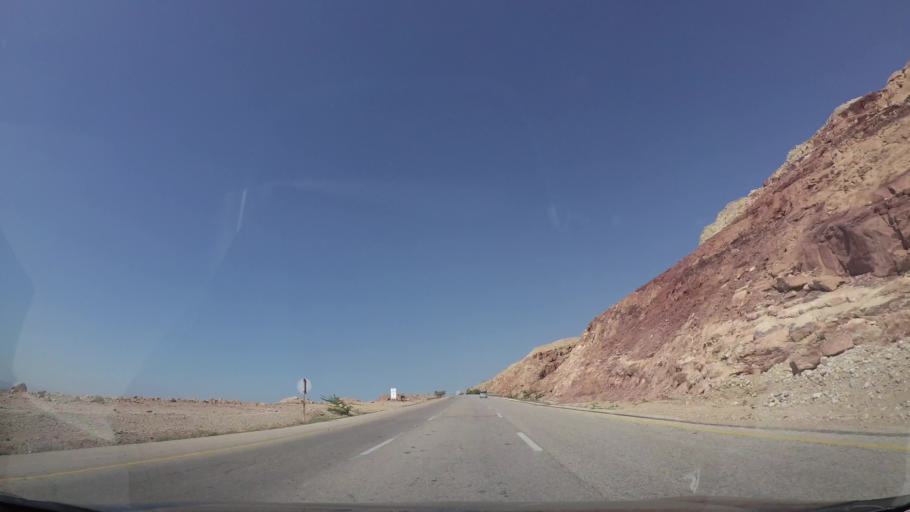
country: JO
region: Madaba
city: Madaba
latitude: 31.5573
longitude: 35.5558
